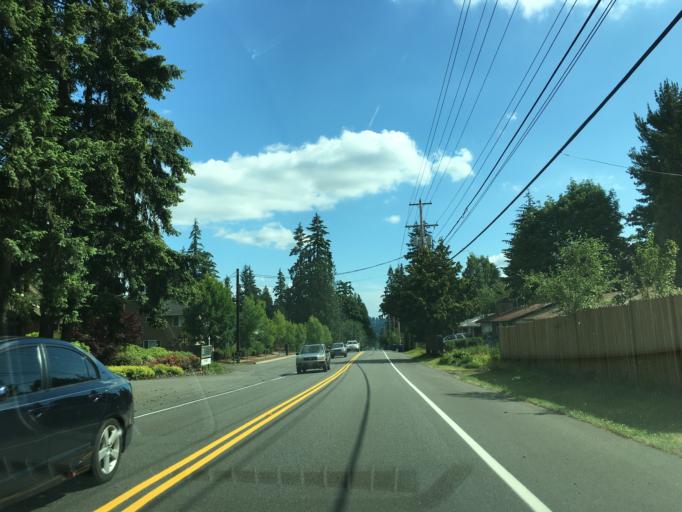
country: US
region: Washington
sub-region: King County
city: Kenmore
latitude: 47.7874
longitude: -122.2331
